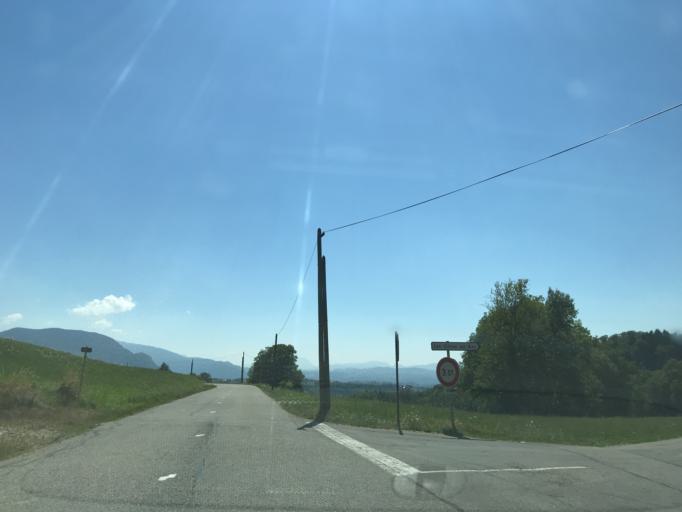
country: FR
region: Rhone-Alpes
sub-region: Departement de la Haute-Savoie
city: Thorens-Glieres
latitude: 45.9747
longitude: 6.2185
